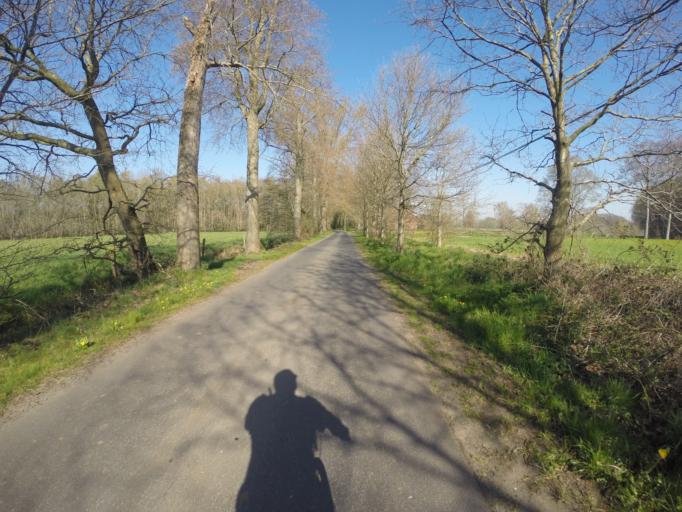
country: BE
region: Flanders
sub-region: Provincie West-Vlaanderen
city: Beernem
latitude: 51.1019
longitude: 3.3673
